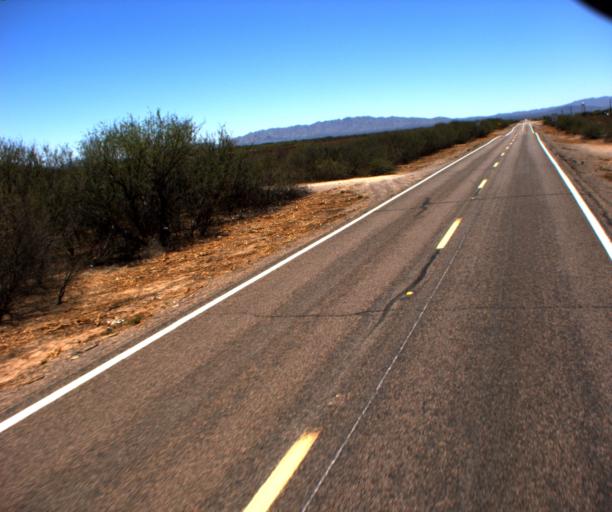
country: US
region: Arizona
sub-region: Pima County
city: Ajo
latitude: 32.1916
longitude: -112.4231
